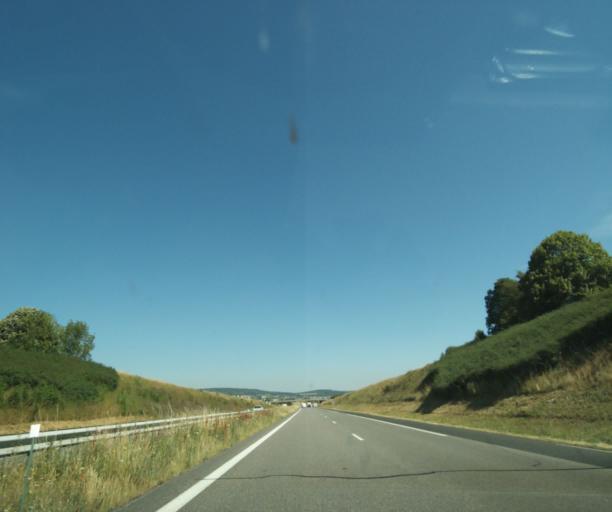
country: FR
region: Lorraine
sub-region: Departement des Vosges
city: Chatenois
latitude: 48.2689
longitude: 5.8613
